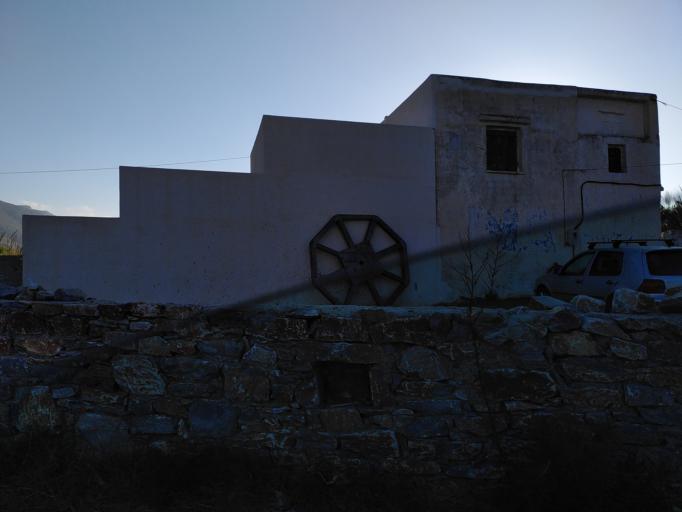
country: GR
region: South Aegean
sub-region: Nomos Kykladon
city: Amorgos
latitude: 36.9057
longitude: 25.9793
